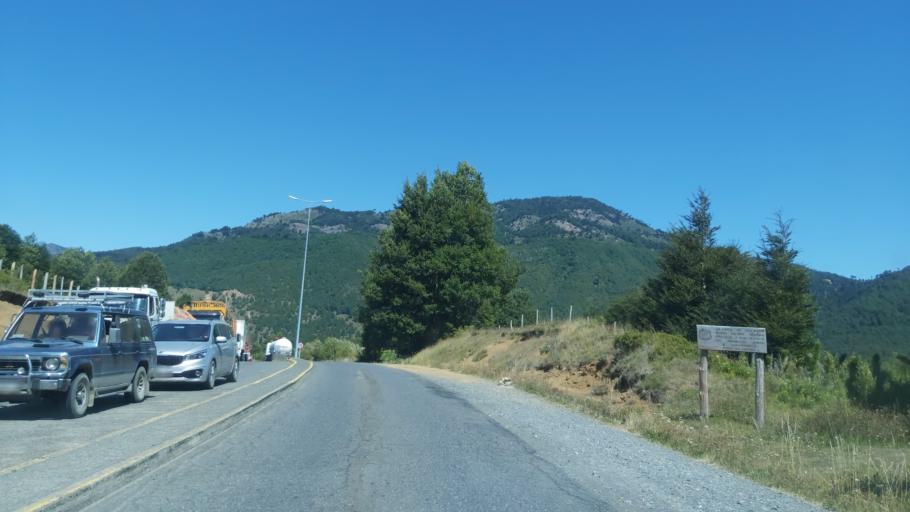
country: CL
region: Araucania
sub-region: Provincia de Cautin
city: Vilcun
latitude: -38.5589
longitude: -71.4973
